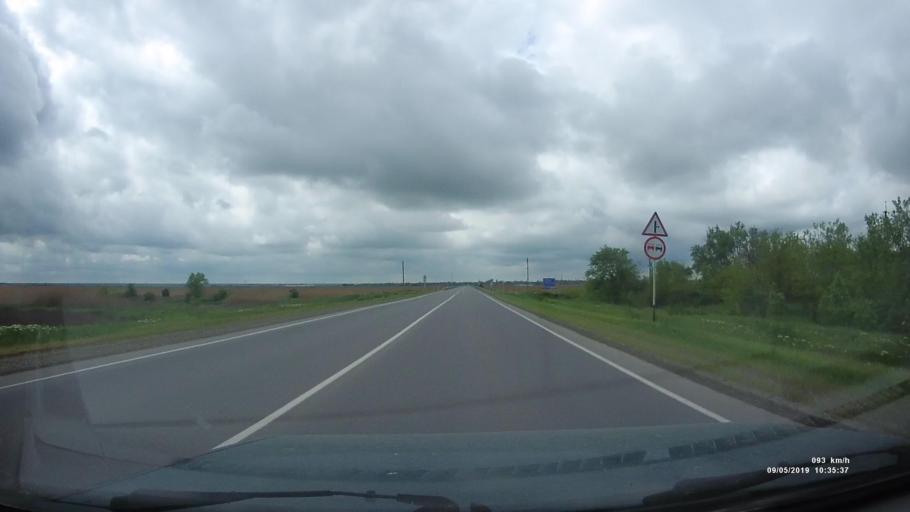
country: RU
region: Rostov
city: Peshkovo
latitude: 47.0403
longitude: 39.4127
